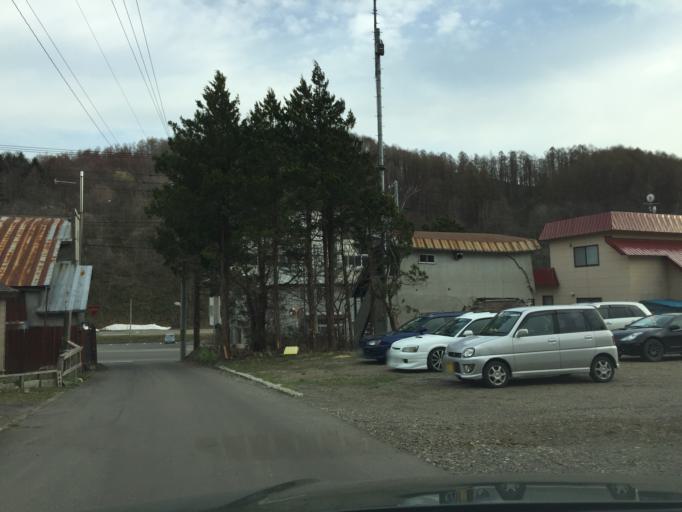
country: JP
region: Hokkaido
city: Utashinai
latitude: 43.5222
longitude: 142.0344
